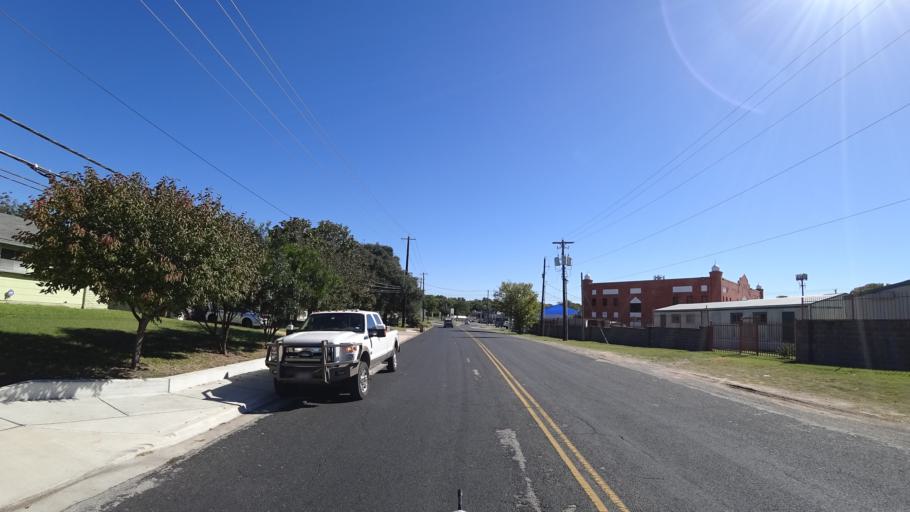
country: US
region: Texas
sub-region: Travis County
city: Austin
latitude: 30.3000
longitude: -97.6873
